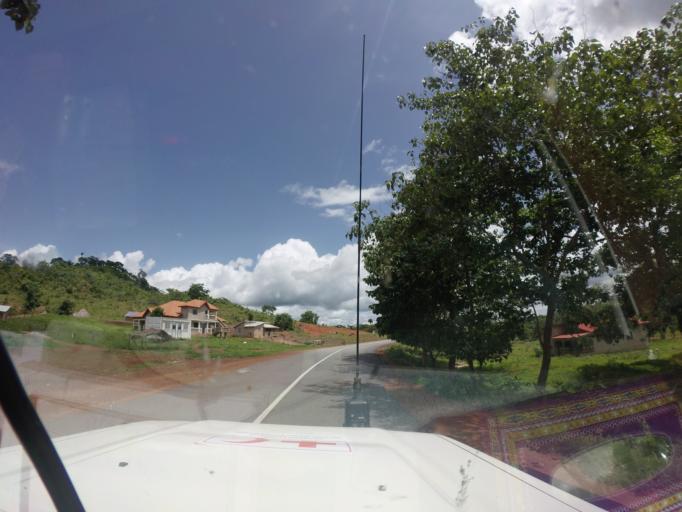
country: SL
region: Northern Province
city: Bindi
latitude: 10.1618
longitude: -11.4211
